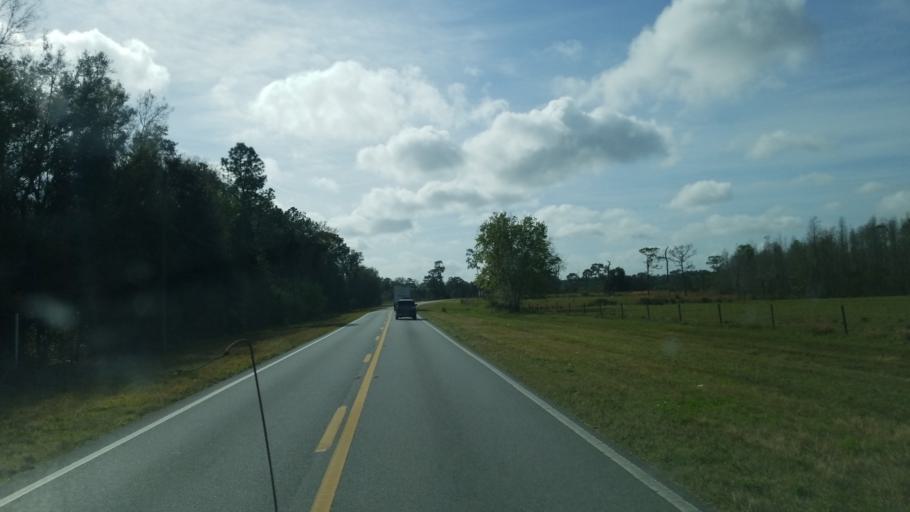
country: US
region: Florida
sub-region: Polk County
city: Polk City
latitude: 28.2395
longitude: -81.7575
